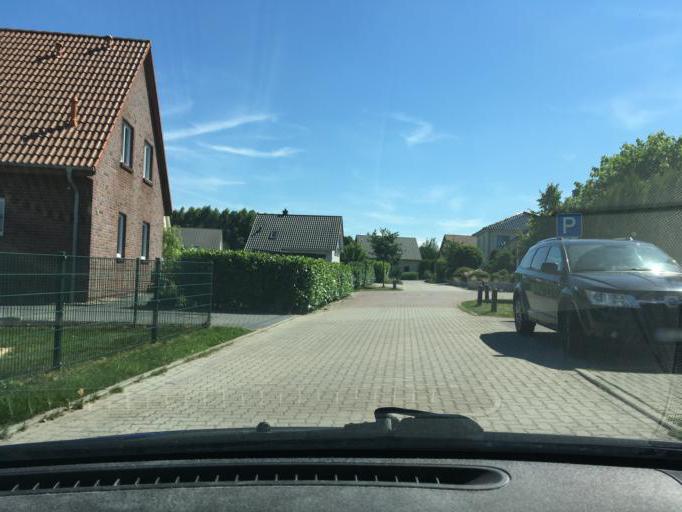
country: DE
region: Lower Saxony
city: Buchholz in der Nordheide
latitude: 53.3769
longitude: 9.8871
